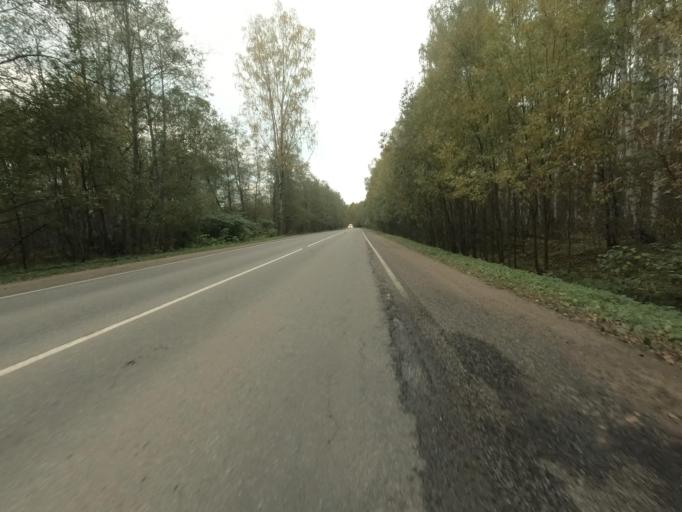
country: RU
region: Leningrad
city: Pavlovo
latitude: 59.7990
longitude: 30.9436
